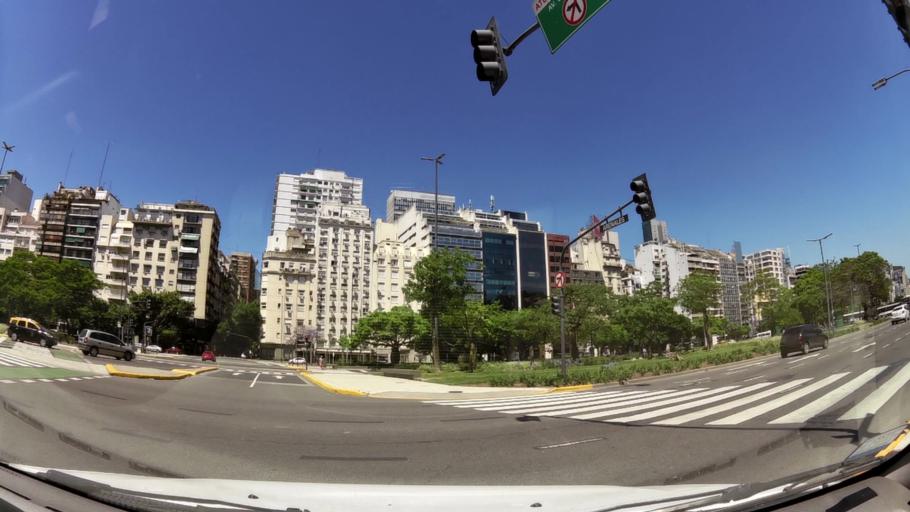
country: AR
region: Buenos Aires F.D.
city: Retiro
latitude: -34.5943
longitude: -58.3827
